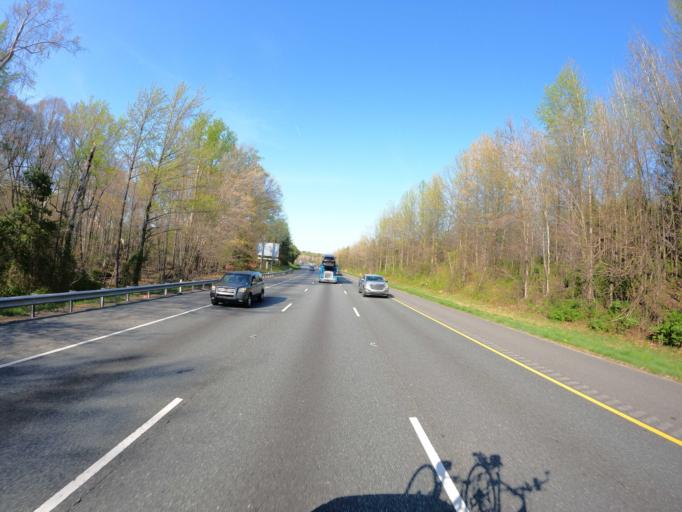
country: US
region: Maryland
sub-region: Harford County
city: Riverside
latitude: 39.4712
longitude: -76.2781
